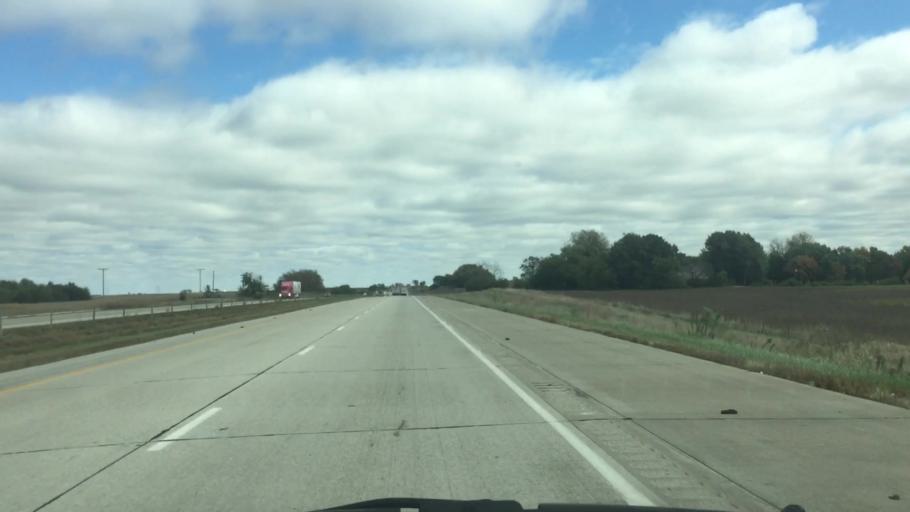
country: US
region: Iowa
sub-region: Polk County
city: Bondurant
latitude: 41.6743
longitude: -93.4299
